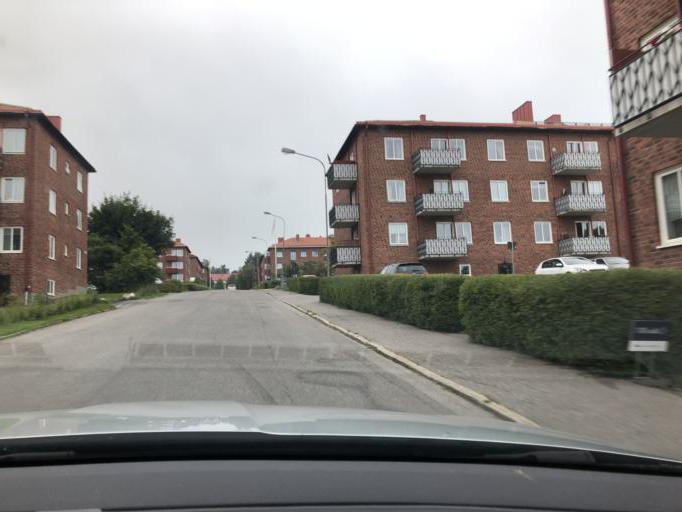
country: SE
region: Vaesternorrland
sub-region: Sundsvalls Kommun
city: Sundsvall
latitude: 62.3990
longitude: 17.3207
